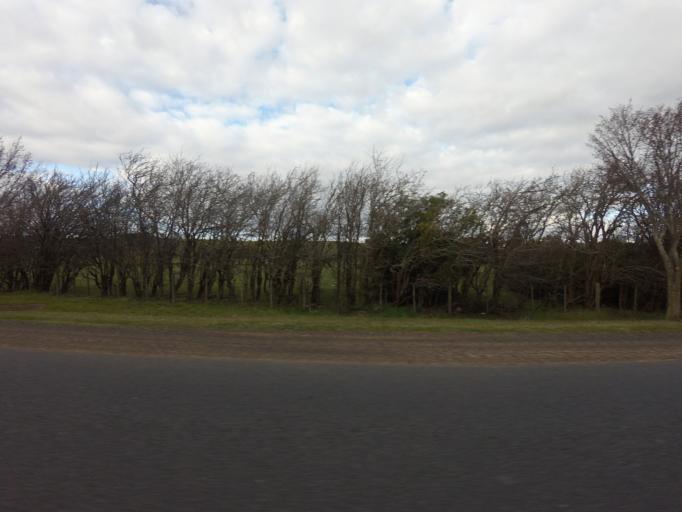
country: AU
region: Tasmania
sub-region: Northern Midlands
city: Evandale
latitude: -42.0177
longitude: 147.4916
